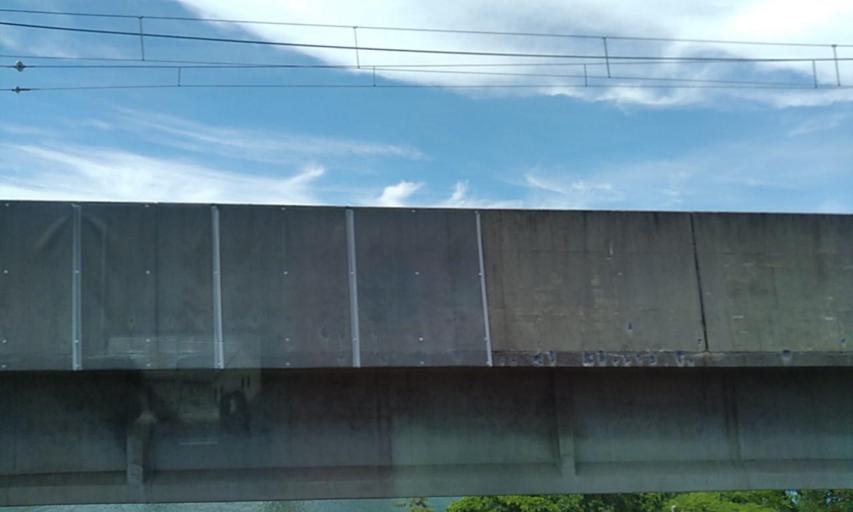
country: JP
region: Kagawa
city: Sakaidecho
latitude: 34.3174
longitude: 133.8220
